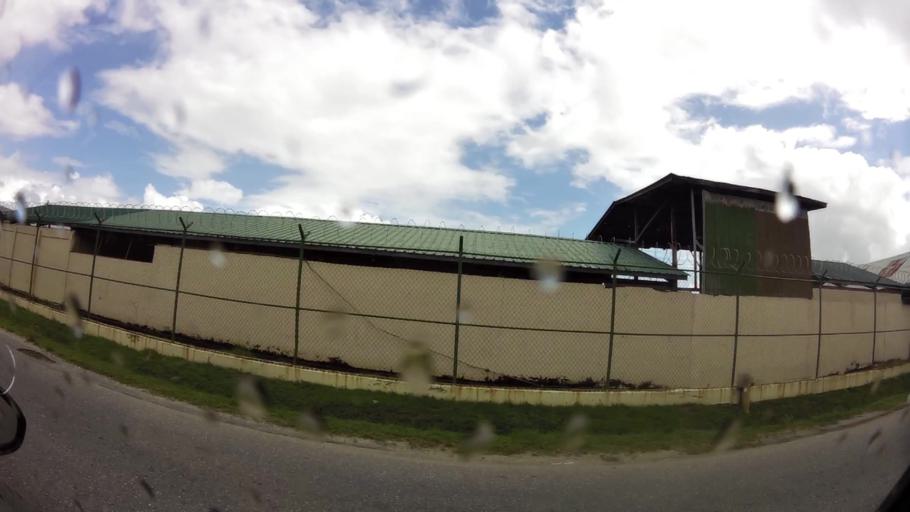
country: TT
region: Tunapuna/Piarco
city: Arouca
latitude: 10.6262
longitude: -61.3391
